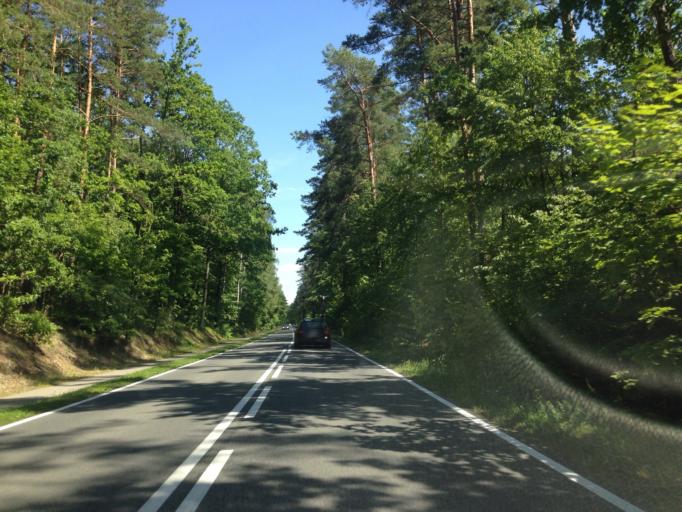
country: PL
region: Kujawsko-Pomorskie
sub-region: Powiat swiecki
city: Osie
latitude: 53.6082
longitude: 18.3094
